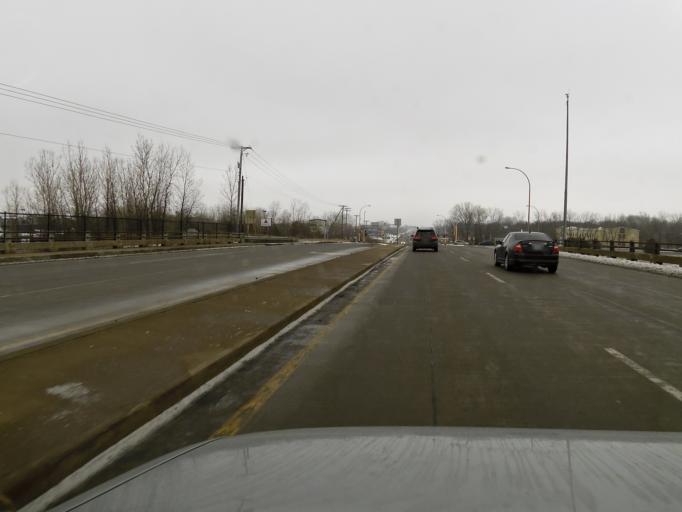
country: US
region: Minnesota
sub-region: Washington County
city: Oakdale
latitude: 44.9632
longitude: -92.9584
